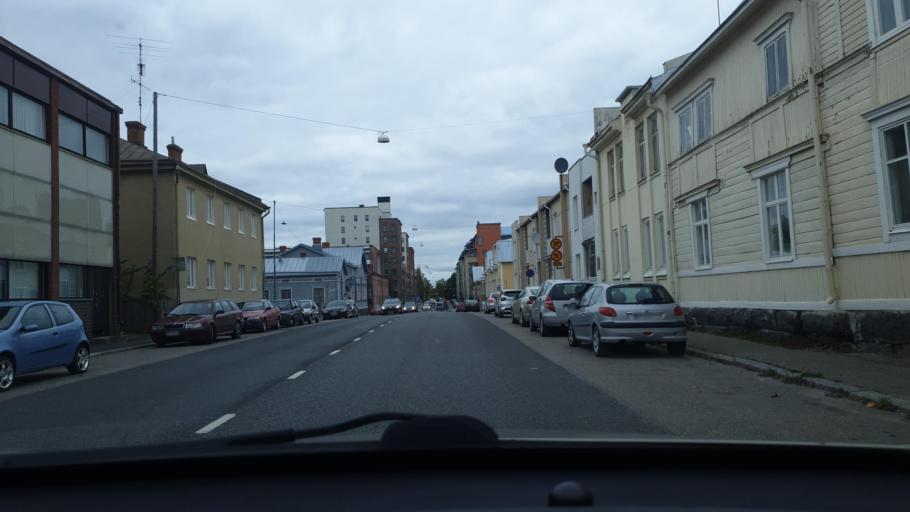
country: FI
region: Ostrobothnia
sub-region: Vaasa
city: Vaasa
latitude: 63.0933
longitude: 21.6246
